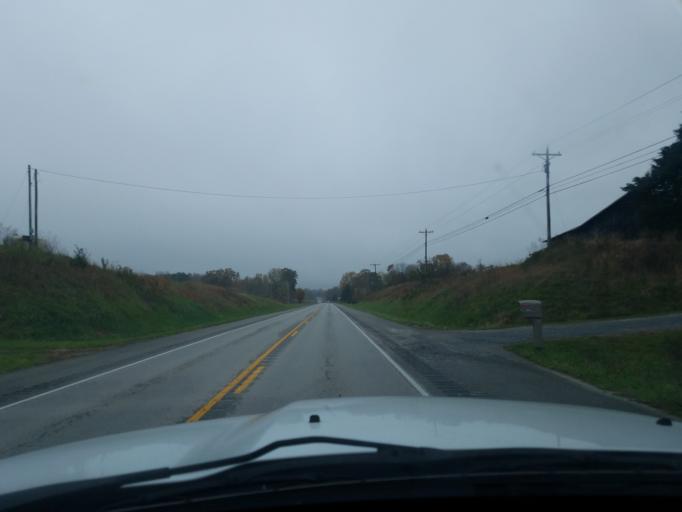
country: US
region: Kentucky
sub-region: Taylor County
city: Campbellsville
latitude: 37.3731
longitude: -85.4061
